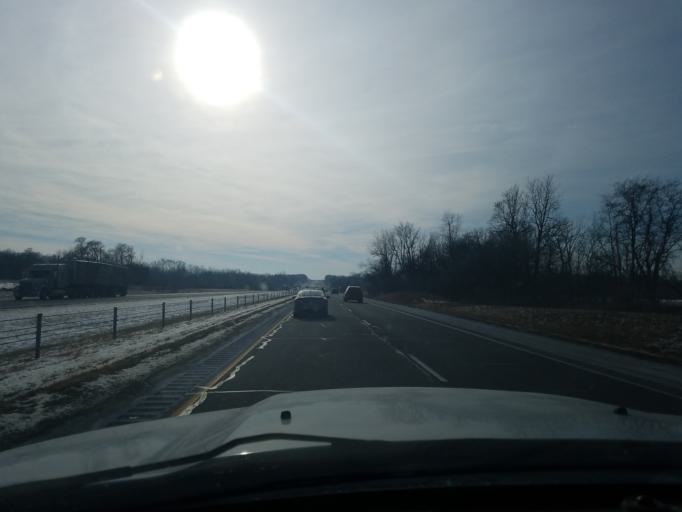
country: US
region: Indiana
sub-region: Huntington County
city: Warren
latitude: 40.7109
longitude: -85.4485
